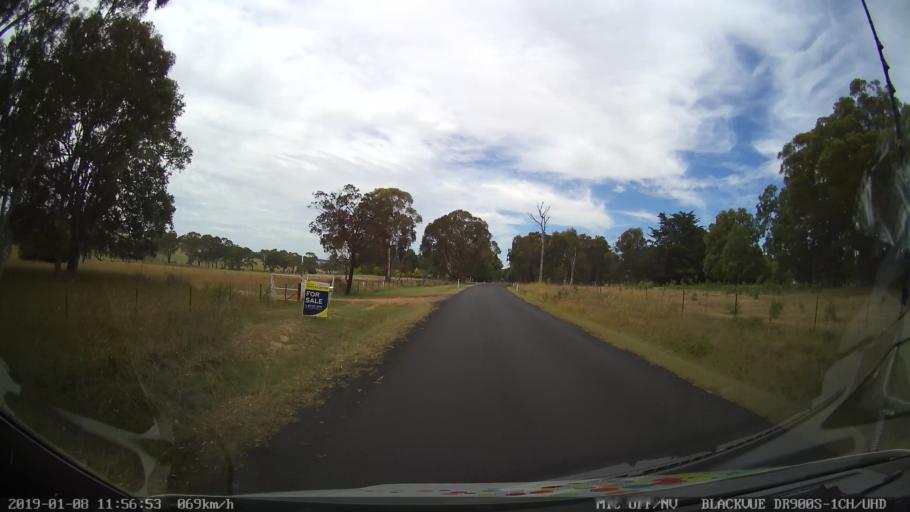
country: AU
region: New South Wales
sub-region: Armidale Dumaresq
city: Armidale
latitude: -30.4449
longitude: 151.5650
